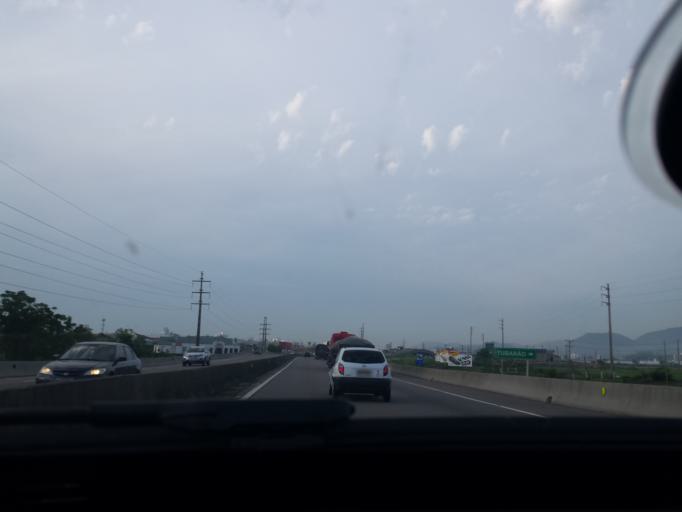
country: BR
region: Santa Catarina
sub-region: Tubarao
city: Tubarao
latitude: -28.4615
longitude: -48.9910
